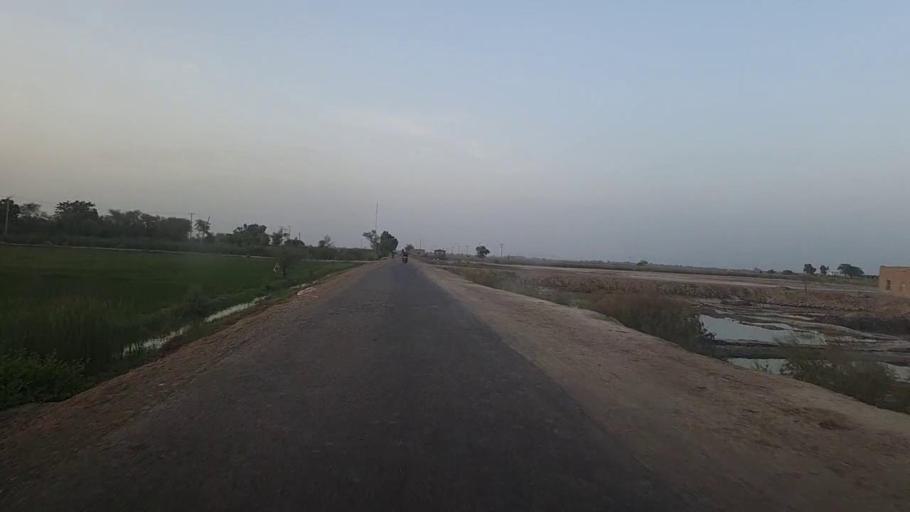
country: PK
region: Sindh
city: Radhan
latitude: 27.1407
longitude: 67.9344
